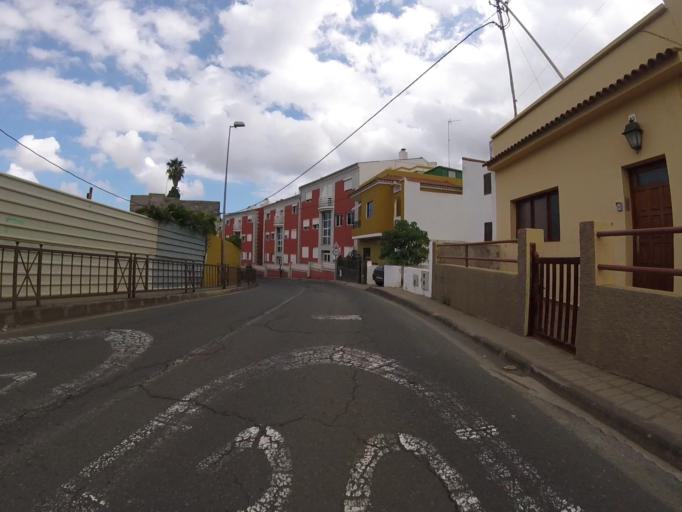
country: ES
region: Canary Islands
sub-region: Provincia de Las Palmas
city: Santa Brigida
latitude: 28.0391
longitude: -15.4924
